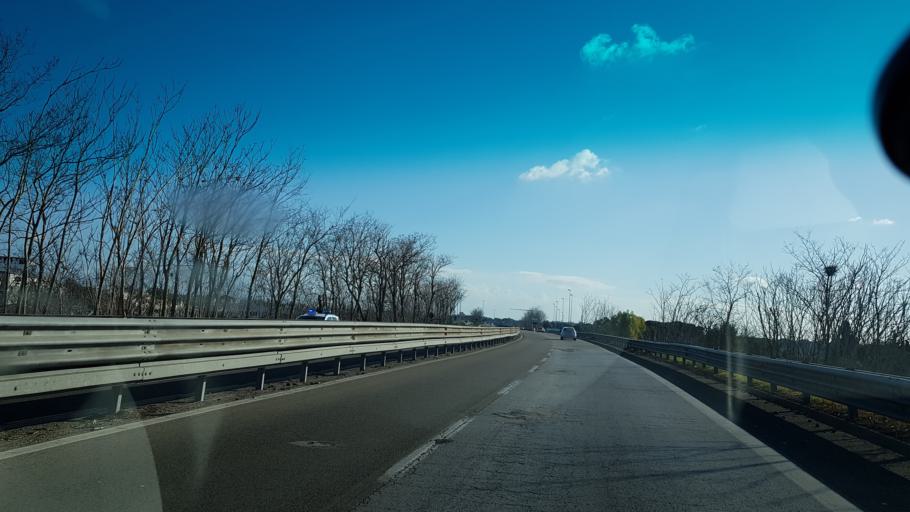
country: IT
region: Apulia
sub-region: Provincia di Lecce
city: Castromediano
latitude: 40.3236
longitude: 18.1729
